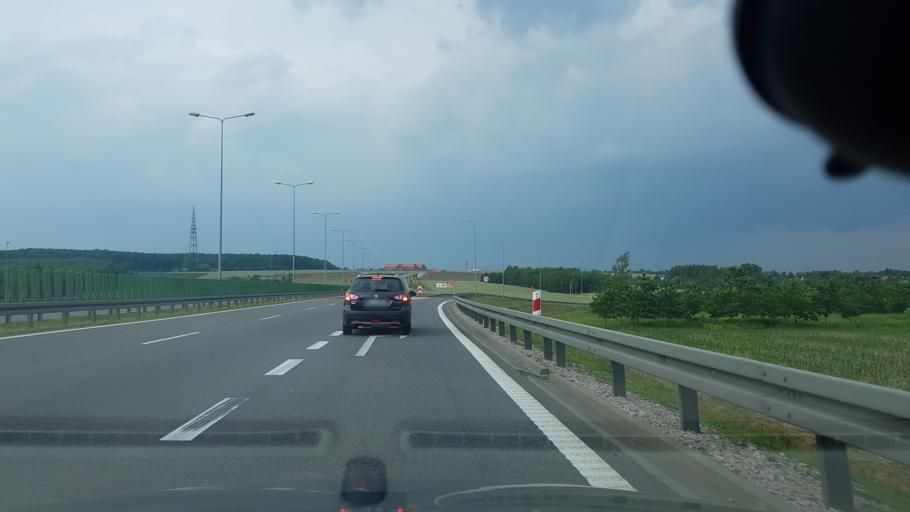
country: PL
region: Masovian Voivodeship
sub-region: Powiat legionowski
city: Serock
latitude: 52.5280
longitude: 21.0581
